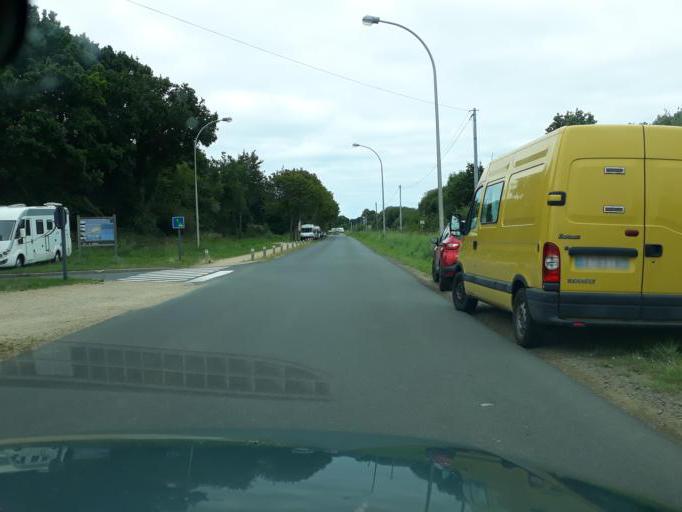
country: FR
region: Brittany
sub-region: Departement des Cotes-d'Armor
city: Paimpol
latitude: 48.7702
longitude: -3.0651
